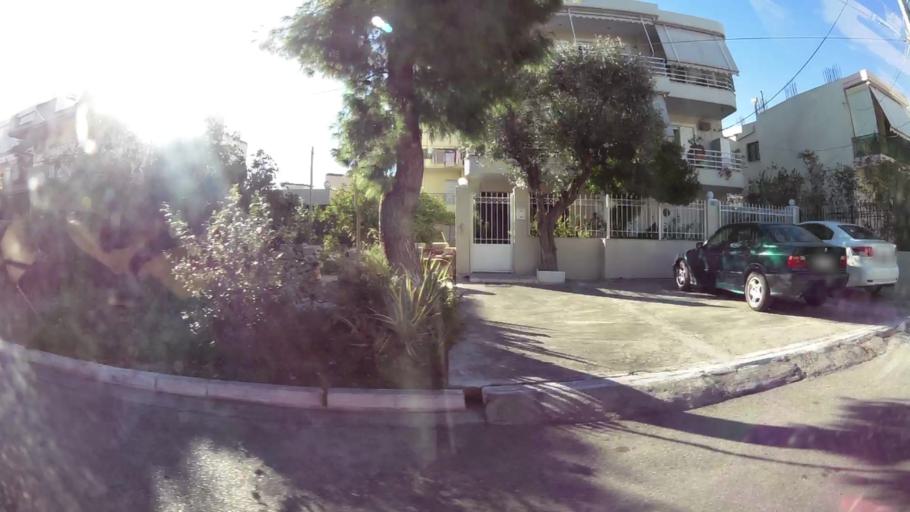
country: GR
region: Attica
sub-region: Nomarchia Anatolikis Attikis
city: Acharnes
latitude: 38.0915
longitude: 23.7356
